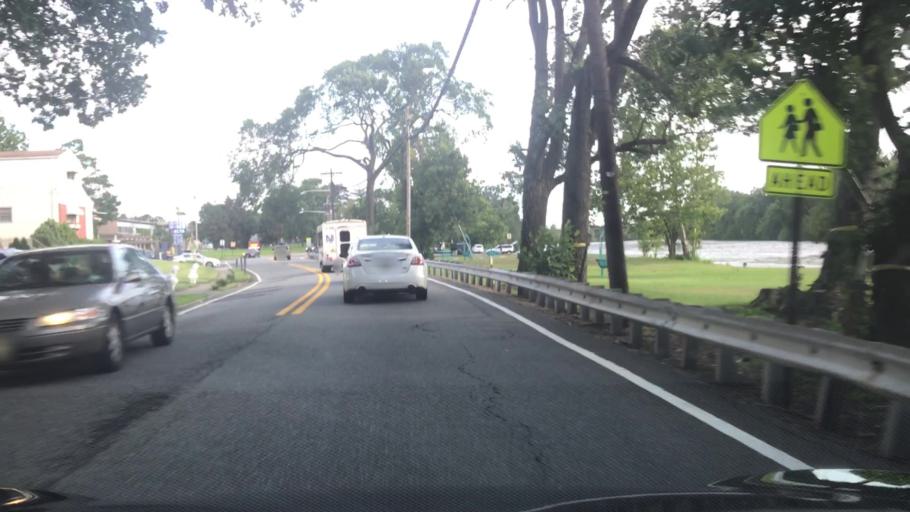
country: US
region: New Jersey
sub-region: Bergen County
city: Elmwood Park
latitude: 40.9109
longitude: -74.1321
